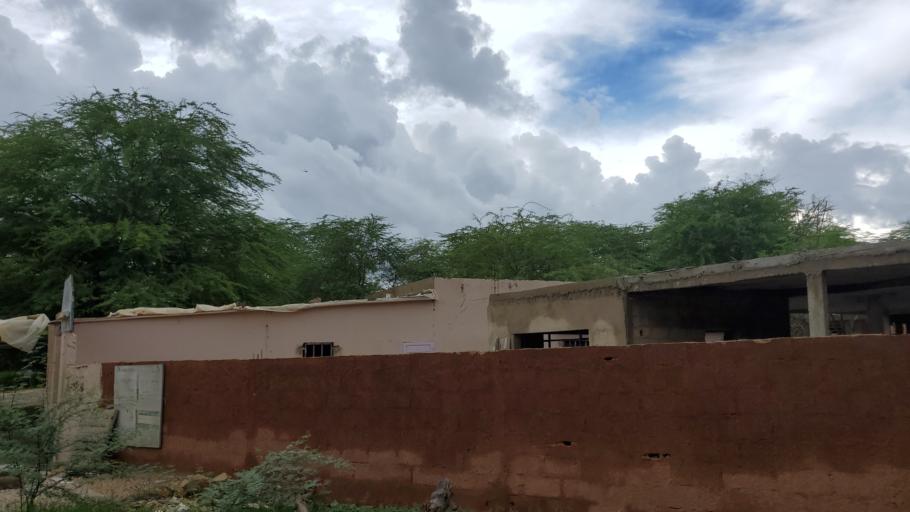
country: SN
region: Saint-Louis
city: Saint-Louis
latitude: 16.0651
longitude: -16.4196
